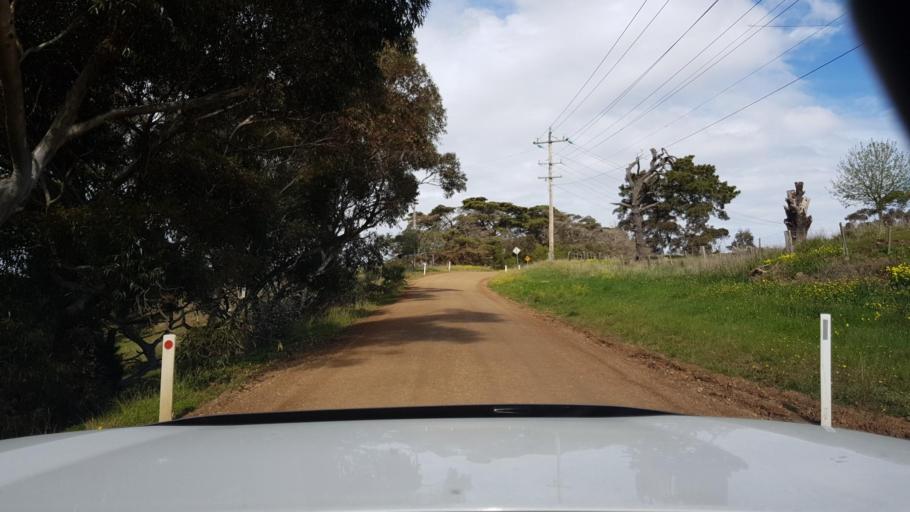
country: AU
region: Victoria
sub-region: Hume
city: Diggers Rest
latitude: -37.5966
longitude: 144.6755
